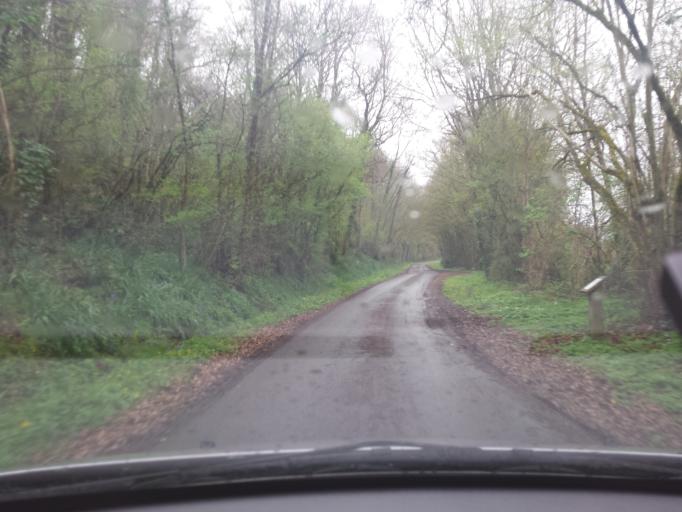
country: FR
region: Pays de la Loire
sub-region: Departement de la Vendee
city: Sainte-Hermine
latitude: 46.5946
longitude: -1.0845
